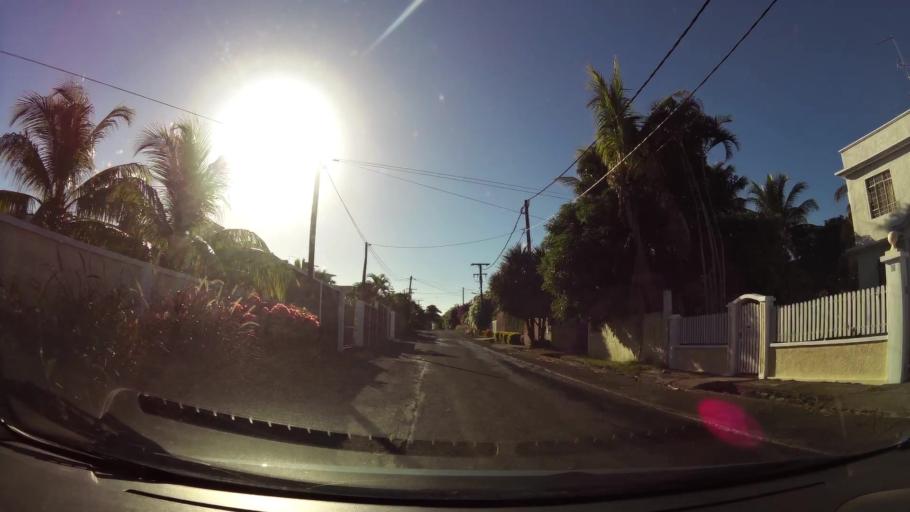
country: MU
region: Black River
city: Tamarin
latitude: -20.3366
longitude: 57.3734
